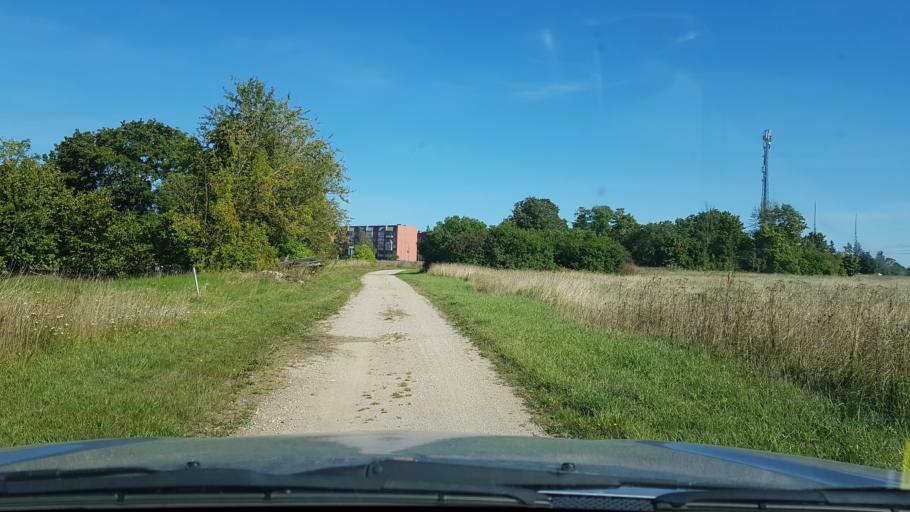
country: EE
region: Ida-Virumaa
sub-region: Sillamaee linn
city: Sillamae
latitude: 59.3890
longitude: 27.7822
